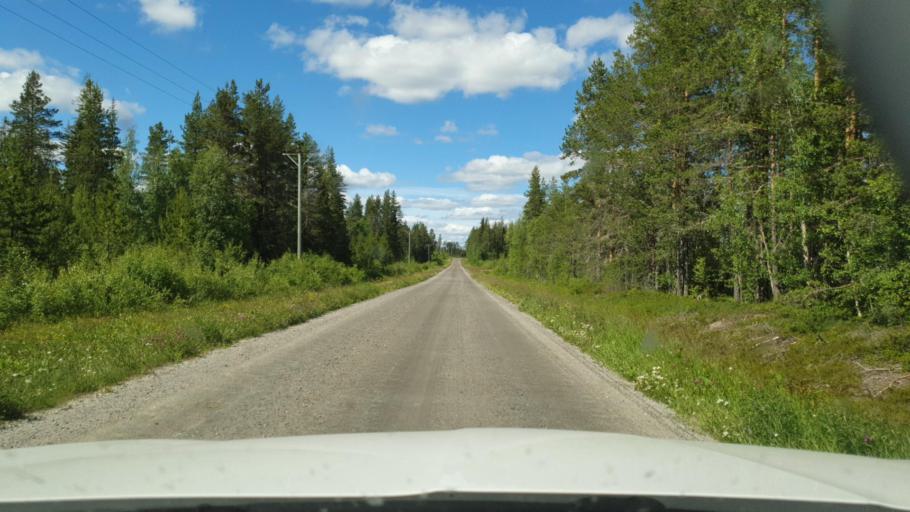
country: SE
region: Vaesterbotten
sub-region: Skelleftea Kommun
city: Backa
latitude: 65.1750
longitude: 21.0934
